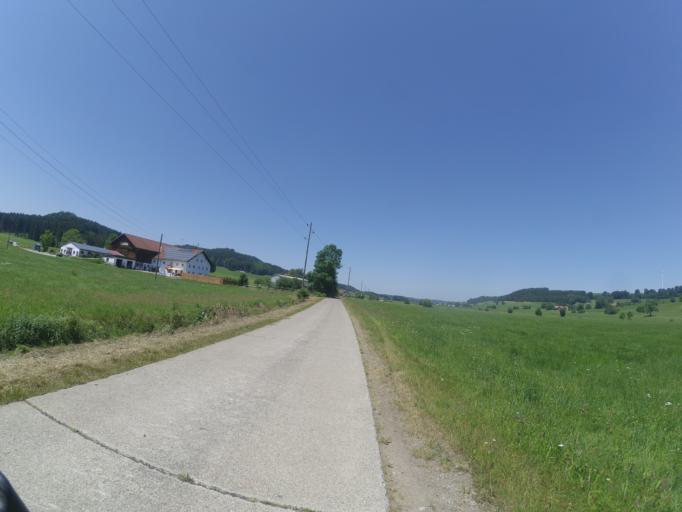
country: DE
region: Bavaria
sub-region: Swabia
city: Untrasried
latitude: 47.8627
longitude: 10.3491
